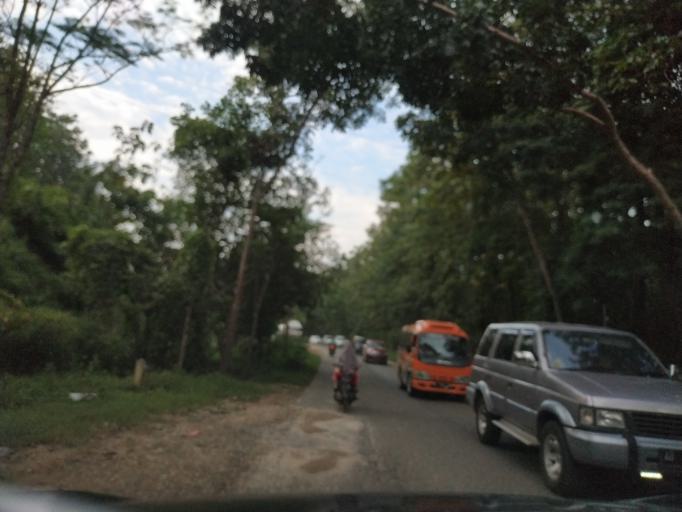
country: ID
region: Central Java
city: Ngampel
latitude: -6.8986
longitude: 111.4400
